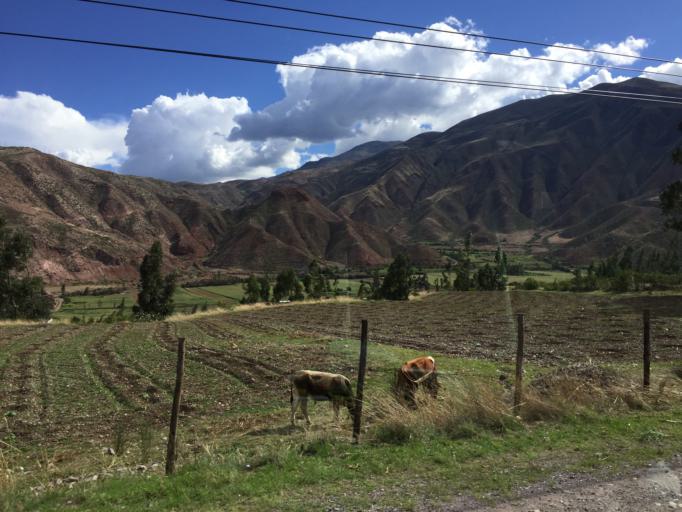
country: PE
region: Cusco
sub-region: Provincia de Urubamba
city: Maras
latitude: -13.2781
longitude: -72.1881
